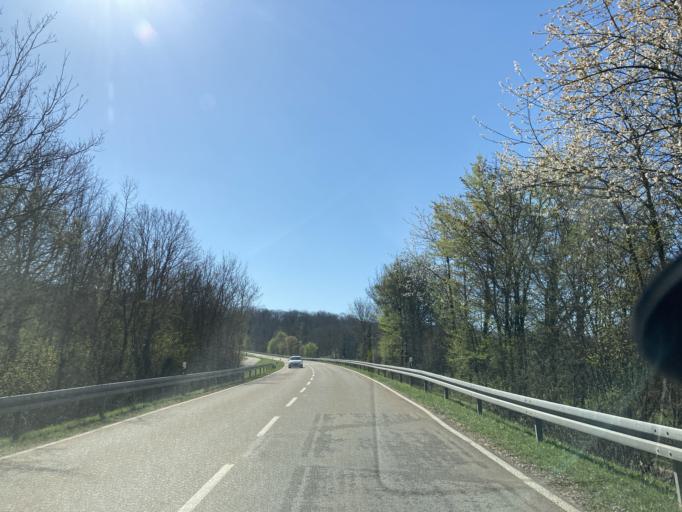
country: DE
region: Baden-Wuerttemberg
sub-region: Freiburg Region
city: Badenweiler
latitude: 47.7976
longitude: 7.6593
